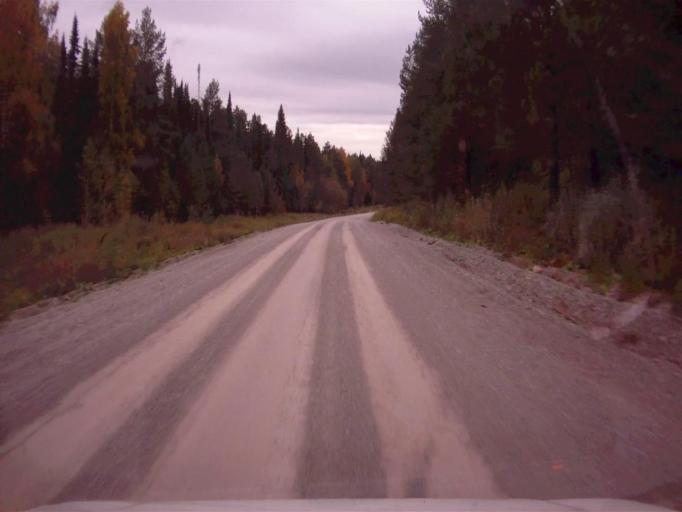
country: RU
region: Chelyabinsk
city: Nyazepetrovsk
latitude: 56.0499
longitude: 59.5304
